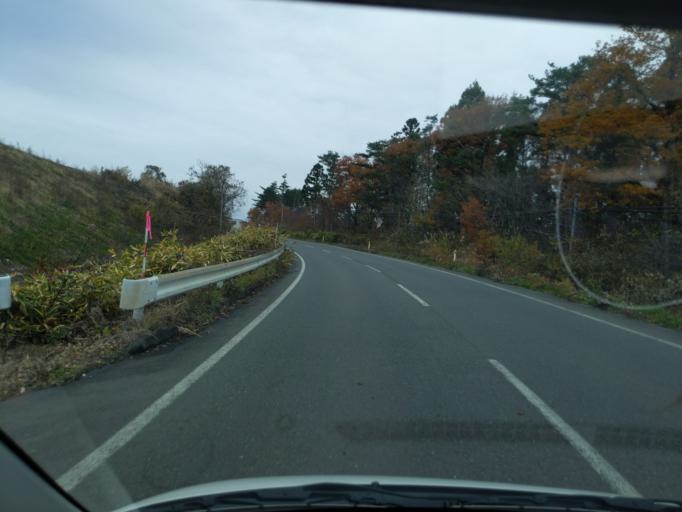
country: JP
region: Iwate
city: Kitakami
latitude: 39.2317
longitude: 141.2222
